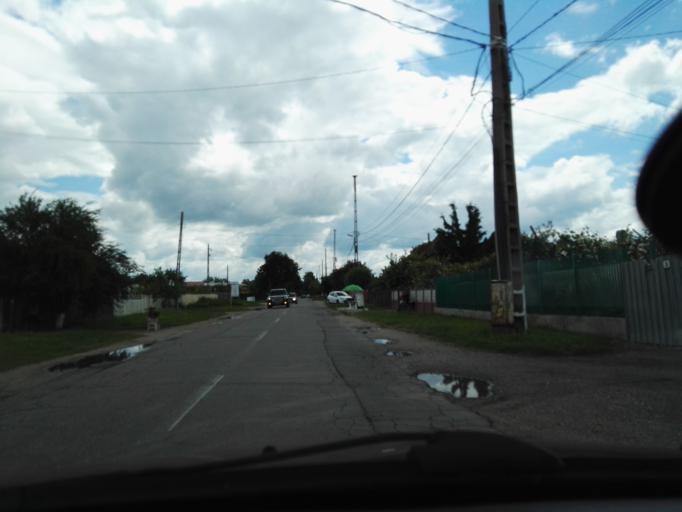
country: RO
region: Ilfov
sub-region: Comuna Copaceni
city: Copaceni
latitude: 44.2423
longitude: 26.1028
